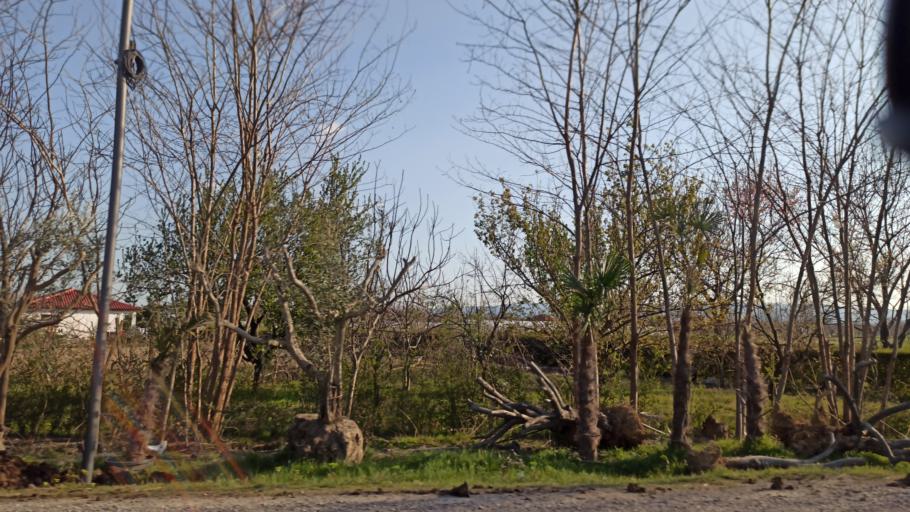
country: AL
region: Shkoder
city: Vukatane
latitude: 41.9930
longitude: 19.5601
